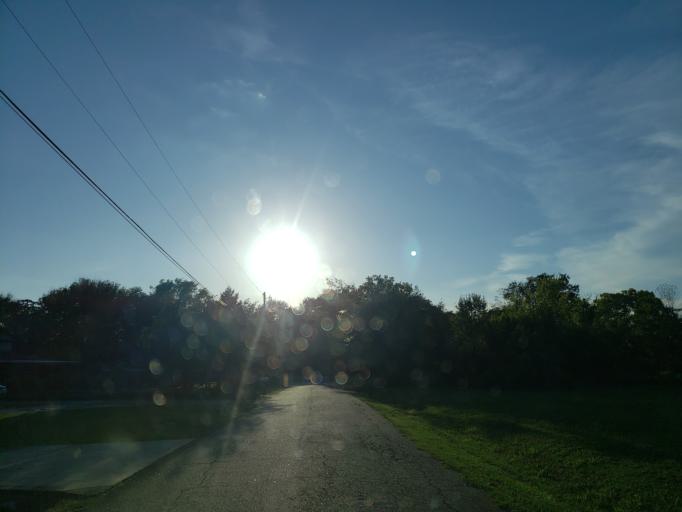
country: US
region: Georgia
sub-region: Bartow County
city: Euharlee
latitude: 34.2345
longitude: -84.9496
